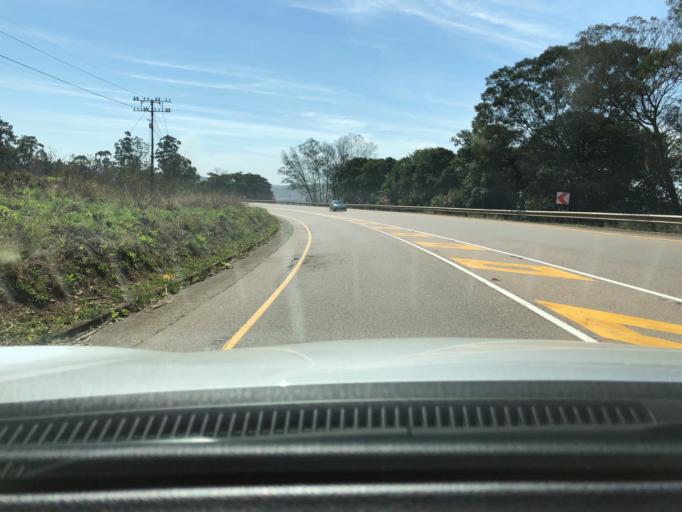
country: ZA
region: KwaZulu-Natal
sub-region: uMgungundlovu District Municipality
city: Richmond
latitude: -29.7868
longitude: 30.3527
